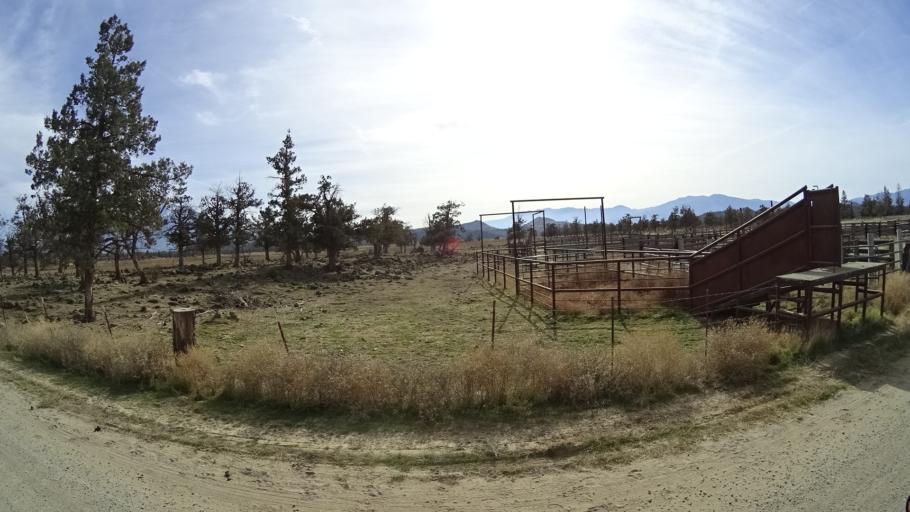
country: US
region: California
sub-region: Siskiyou County
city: Montague
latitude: 41.5952
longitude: -122.4232
